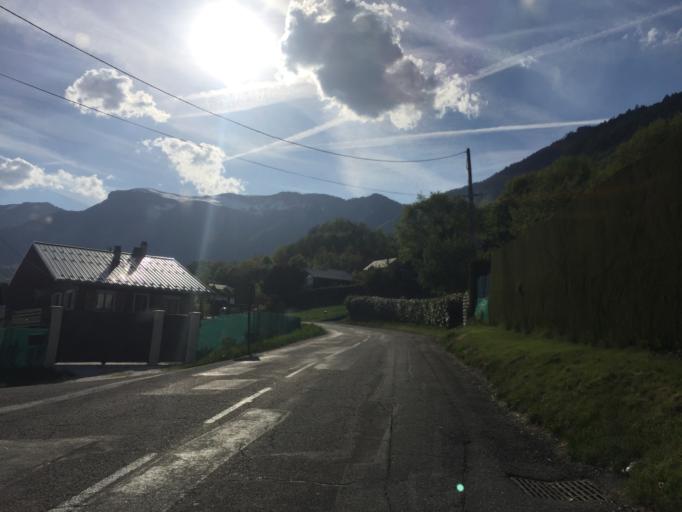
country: FR
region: Rhone-Alpes
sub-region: Departement de la Savoie
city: Mercury
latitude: 45.6644
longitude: 6.3199
